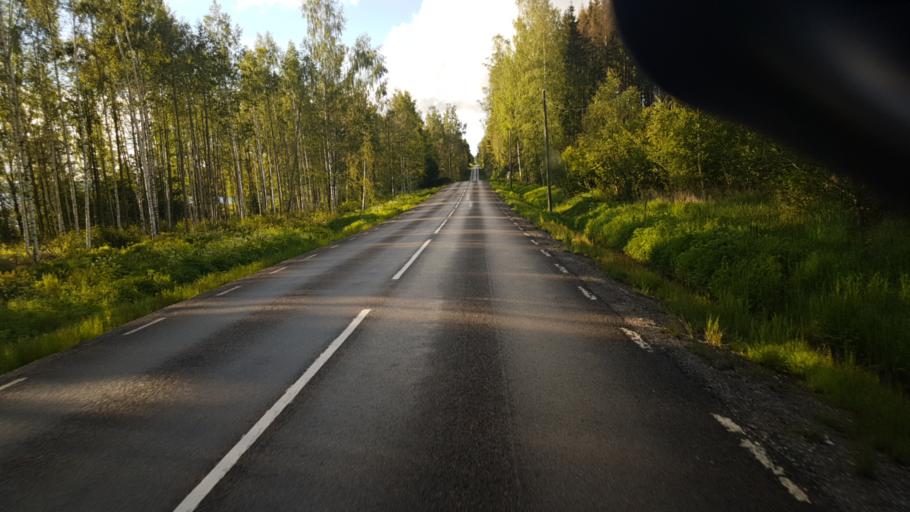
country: SE
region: Vaermland
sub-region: Arvika Kommun
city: Arvika
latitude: 59.6307
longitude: 12.4939
